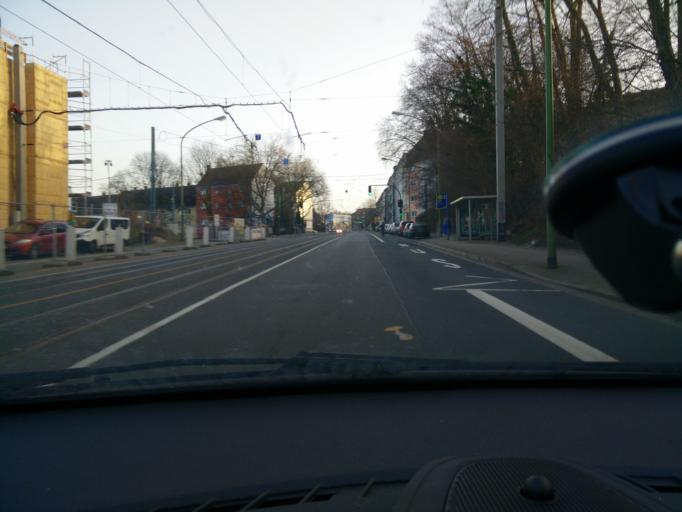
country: DE
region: North Rhine-Westphalia
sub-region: Regierungsbezirk Dusseldorf
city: Essen
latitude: 51.4604
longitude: 7.0210
